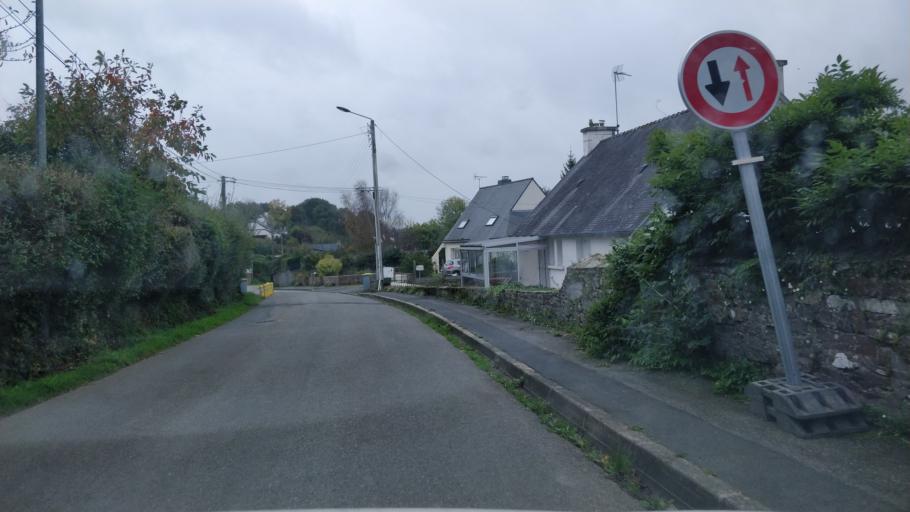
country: FR
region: Brittany
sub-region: Departement des Cotes-d'Armor
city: Lannion
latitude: 48.7399
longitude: -3.4554
